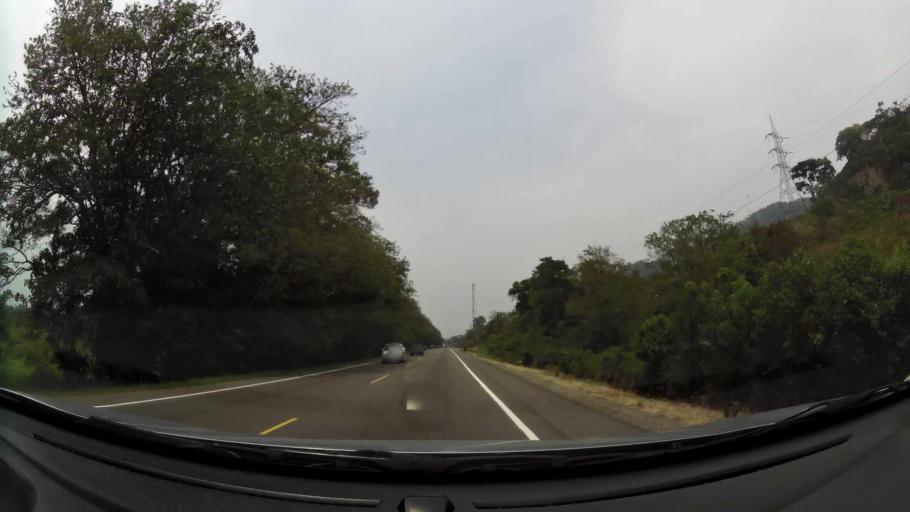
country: HN
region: Cortes
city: La Guama
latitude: 14.8380
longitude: -87.9595
